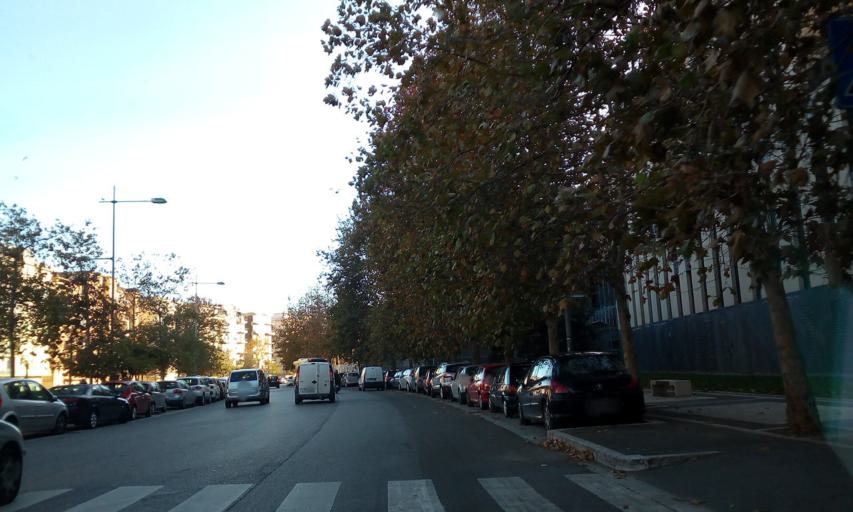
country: IT
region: Campania
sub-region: Provincia di Salerno
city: Salerno
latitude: 40.6788
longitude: 14.7746
